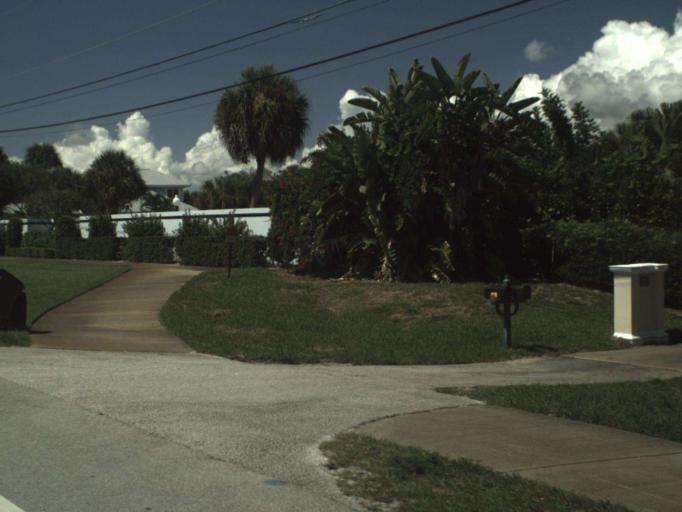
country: US
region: Florida
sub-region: Indian River County
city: South Beach
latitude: 27.5734
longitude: -80.3289
